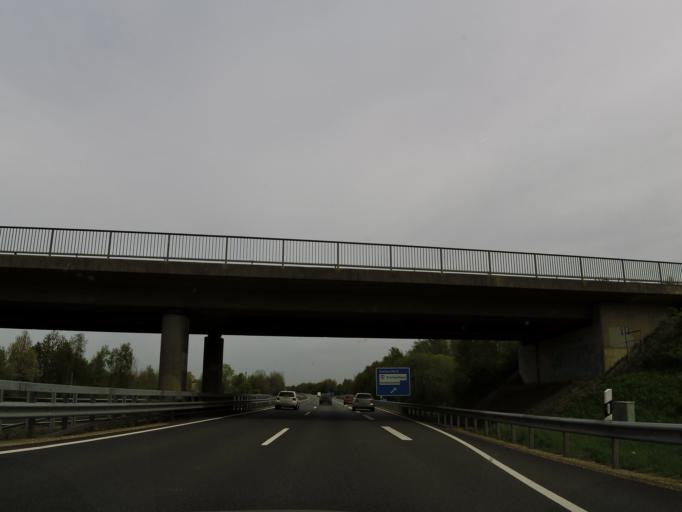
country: DE
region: Schleswig-Holstein
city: Ottenbuttel
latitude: 53.9565
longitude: 9.4903
